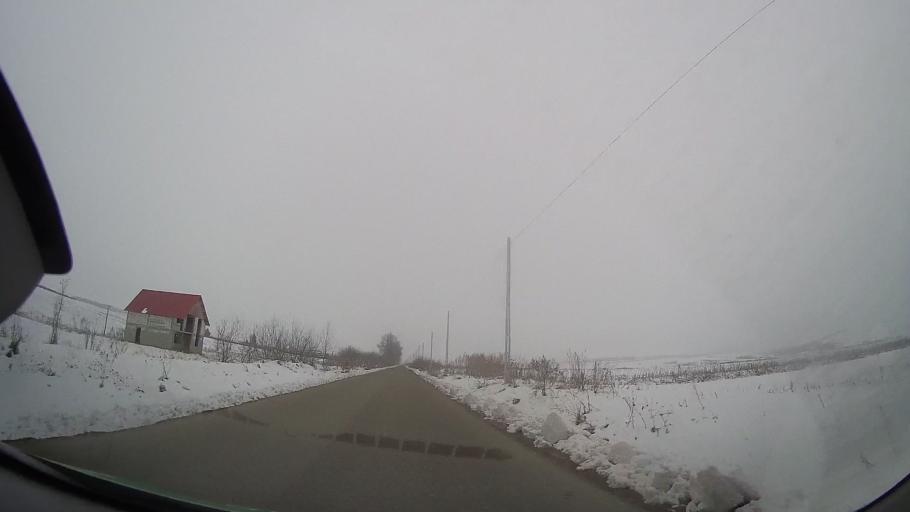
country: RO
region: Vaslui
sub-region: Comuna Todiresti
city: Todiresti
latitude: 46.8458
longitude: 27.3962
